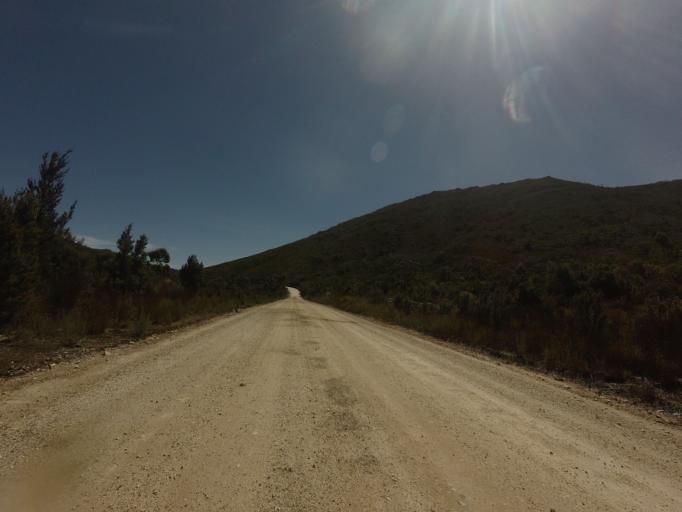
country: AU
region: Tasmania
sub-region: Huon Valley
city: Geeveston
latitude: -42.9363
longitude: 146.3473
